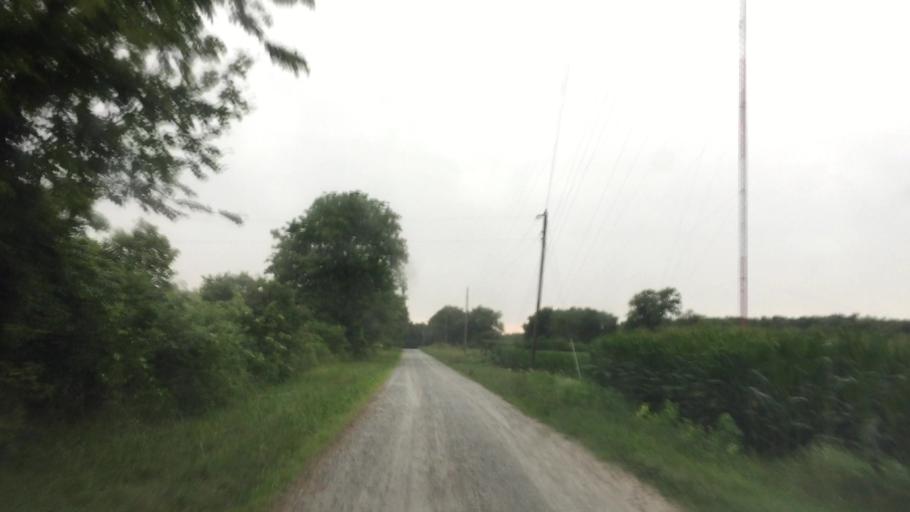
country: US
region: Iowa
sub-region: Lee County
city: Fort Madison
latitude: 40.6065
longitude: -91.2707
